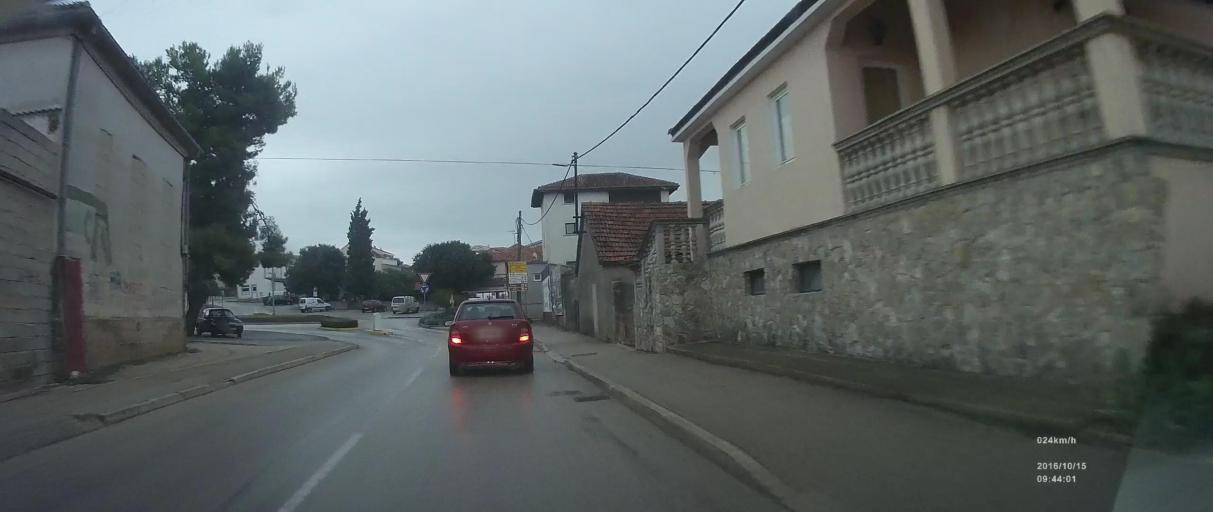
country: HR
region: Zadarska
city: Pakostane
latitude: 43.9100
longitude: 15.5069
